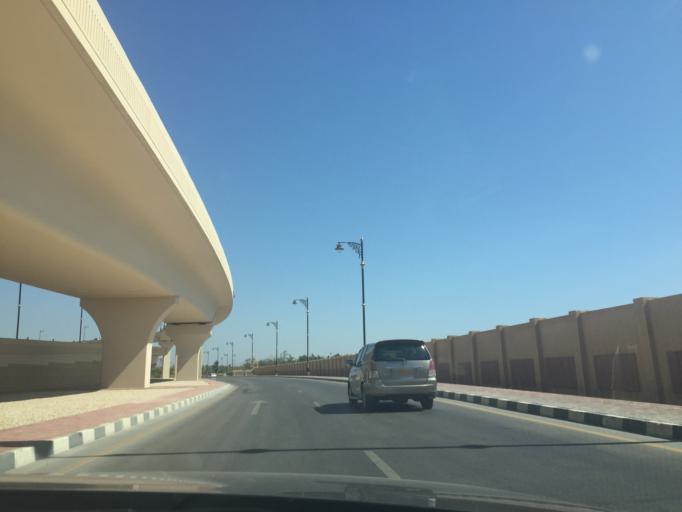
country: OM
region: Zufar
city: Salalah
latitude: 17.0307
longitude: 54.1393
